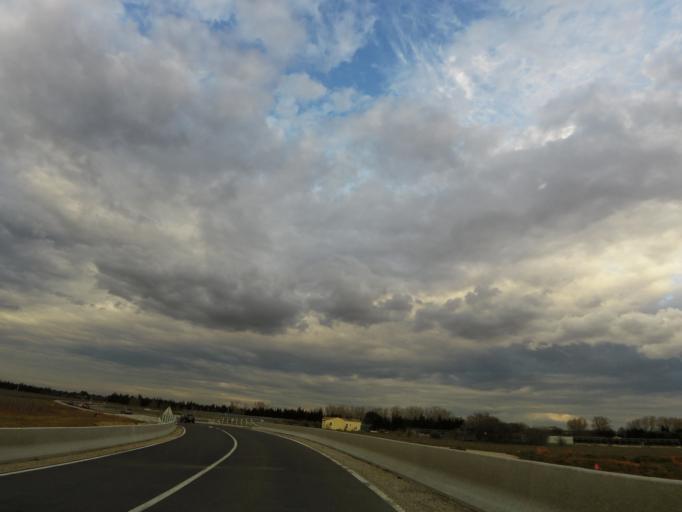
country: FR
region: Languedoc-Roussillon
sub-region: Departement du Gard
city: Vestric-et-Candiac
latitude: 43.7247
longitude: 4.2557
